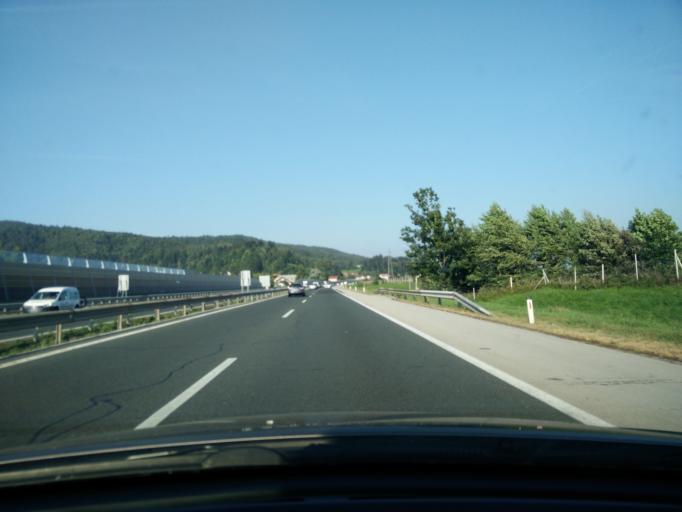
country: SI
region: Log-Dragomer
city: Dragomer
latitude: 46.0124
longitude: 14.3789
